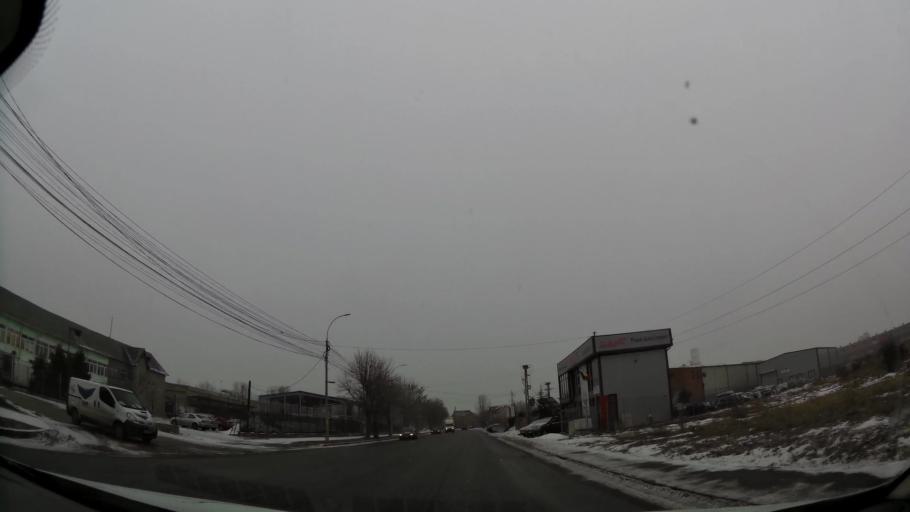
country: RO
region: Dambovita
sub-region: Municipiul Targoviste
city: Targoviste
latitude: 44.9139
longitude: 25.4429
